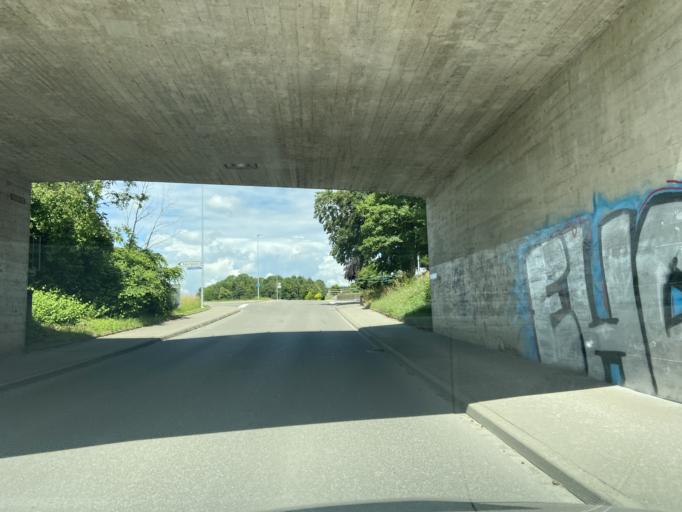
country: CH
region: Zurich
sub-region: Bezirk Winterthur
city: Oberwinterthur (Kreis 2)
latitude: 47.5264
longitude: 8.7769
